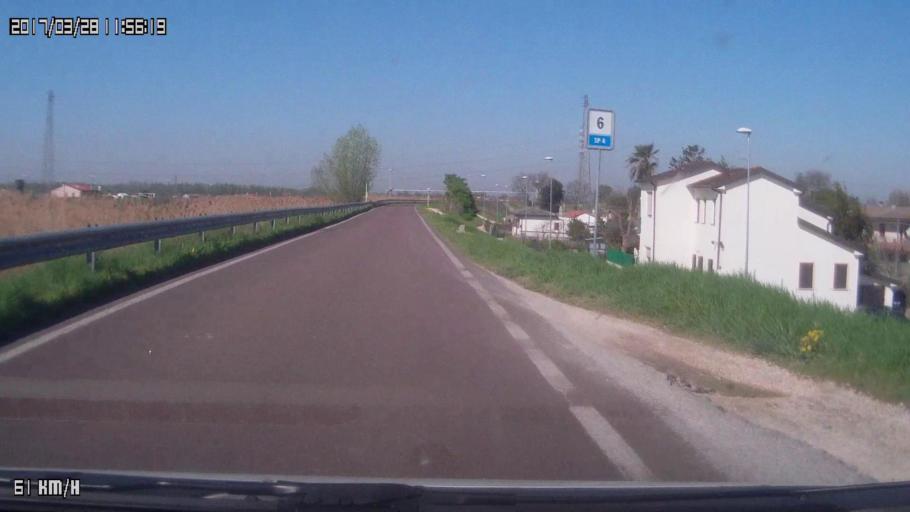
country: IT
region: Veneto
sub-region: Provincia di Venezia
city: Boscochiaro
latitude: 45.1329
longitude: 12.1396
